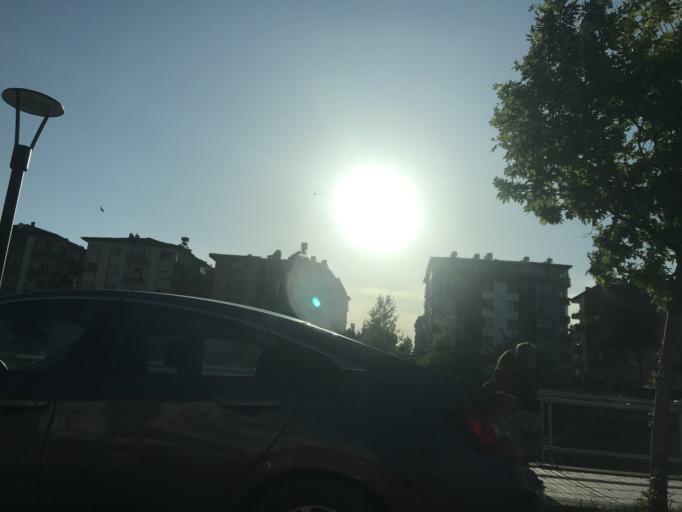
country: TR
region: Hatay
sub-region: Antakya Ilcesi
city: Antakya
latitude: 36.2093
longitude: 36.1623
